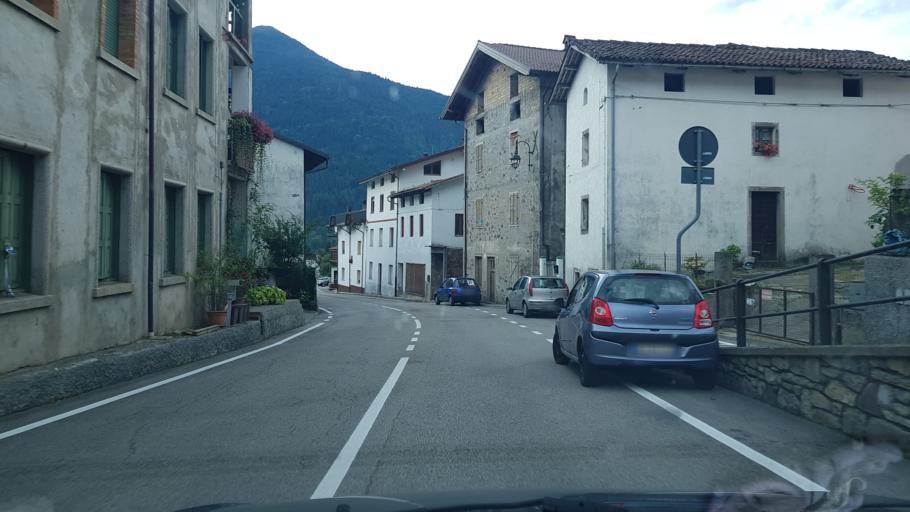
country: IT
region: Friuli Venezia Giulia
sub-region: Provincia di Udine
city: Cercivento
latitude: 46.5272
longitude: 12.9943
